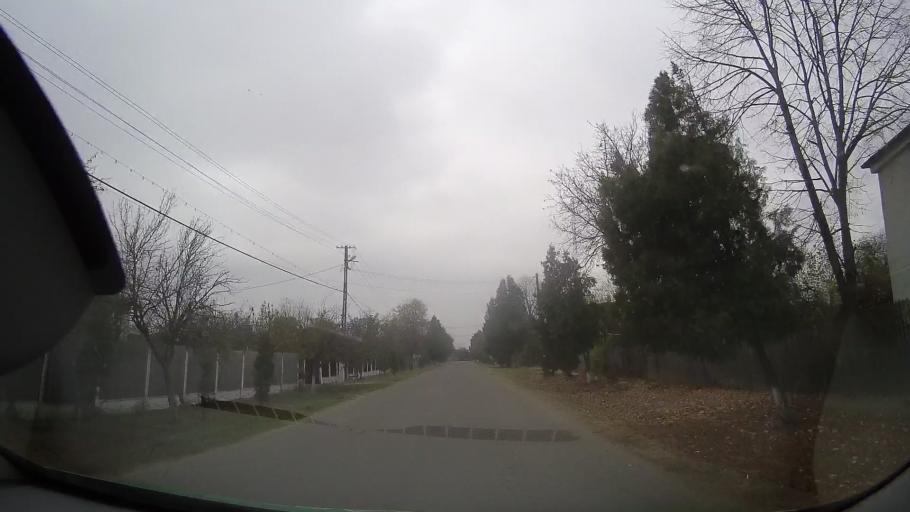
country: RO
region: Buzau
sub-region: Comuna Scutelnici
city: Scutelnici
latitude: 44.8481
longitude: 26.9202
